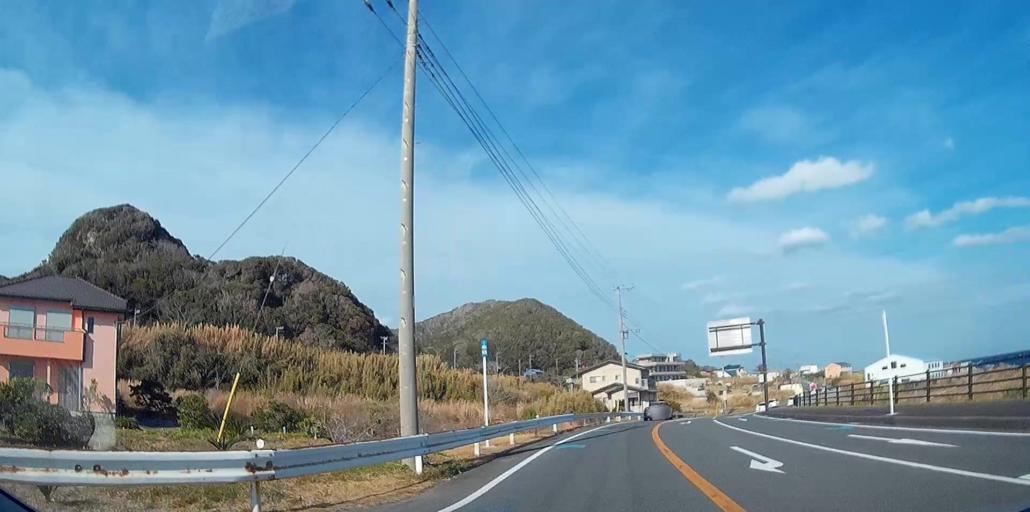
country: JP
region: Chiba
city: Tateyama
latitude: 34.9142
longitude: 139.9322
